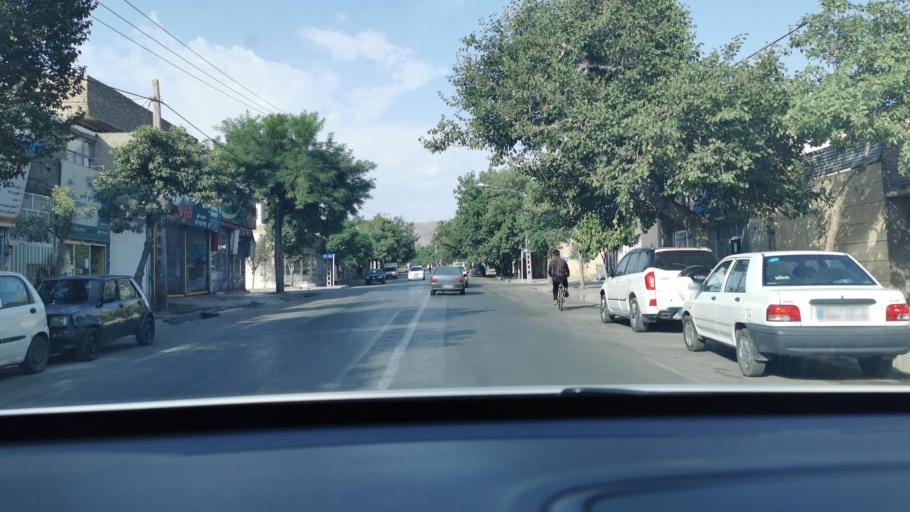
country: IR
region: Razavi Khorasan
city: Mashhad
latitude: 36.2585
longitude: 59.6122
